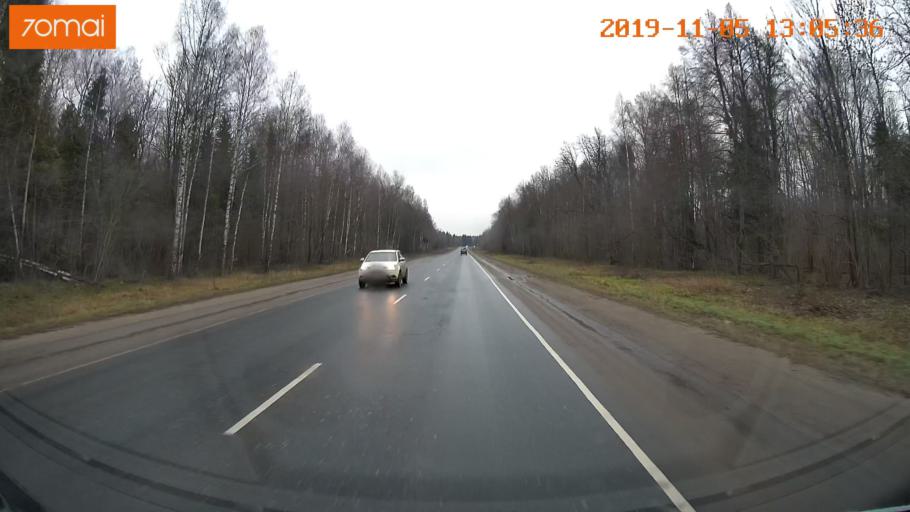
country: RU
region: Ivanovo
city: Kitovo
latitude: 56.8814
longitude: 41.2465
